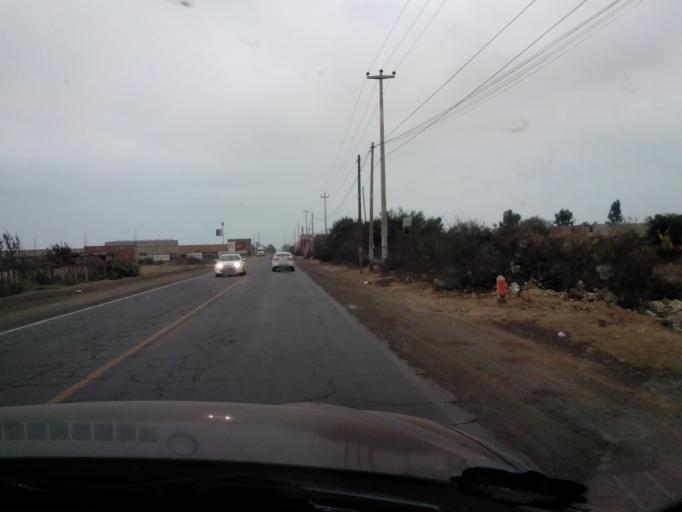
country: PE
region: Ica
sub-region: Provincia de Chincha
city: San Pedro
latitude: -13.4099
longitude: -76.1705
